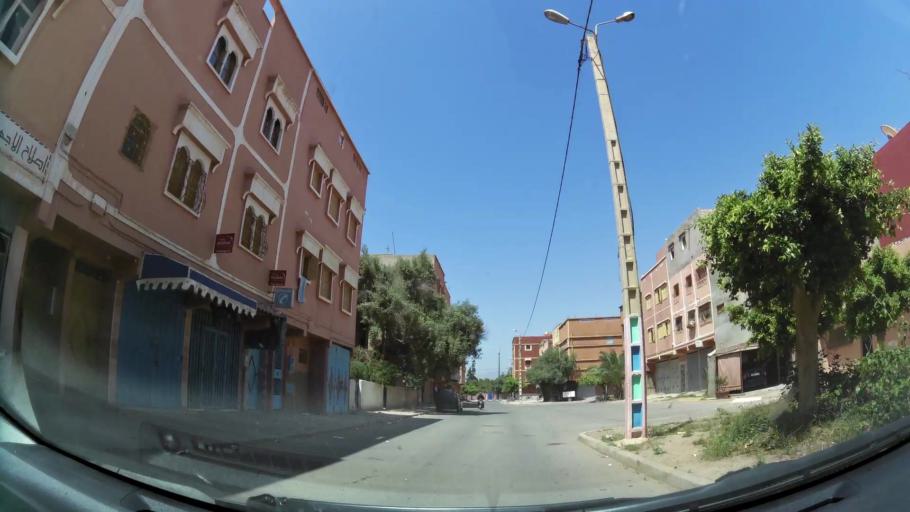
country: MA
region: Souss-Massa-Draa
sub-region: Inezgane-Ait Mellou
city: Inezgane
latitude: 30.3461
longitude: -9.4860
